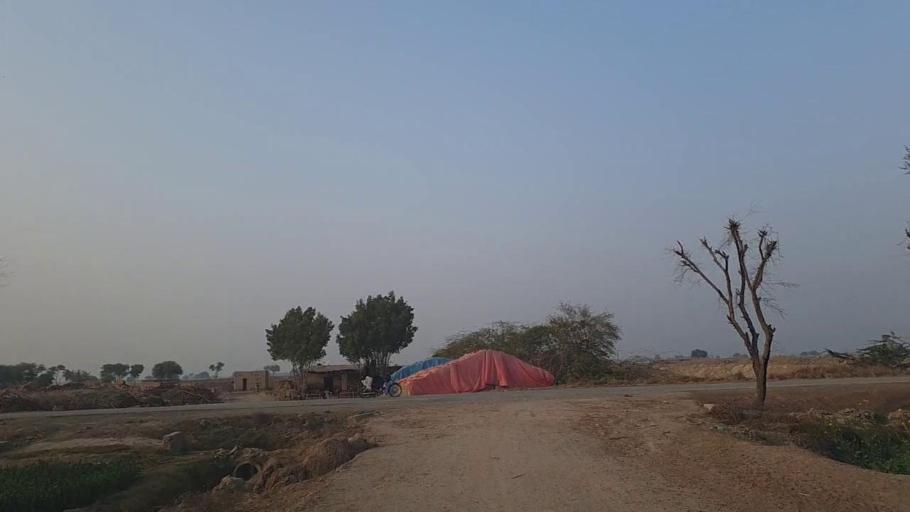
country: PK
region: Sindh
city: Nawabshah
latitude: 26.2566
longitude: 68.4711
